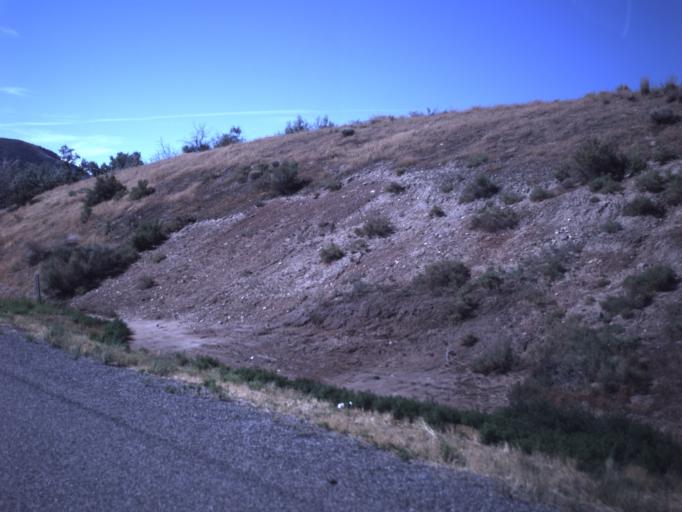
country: US
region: Utah
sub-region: Sevier County
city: Salina
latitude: 38.9462
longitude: -111.8567
